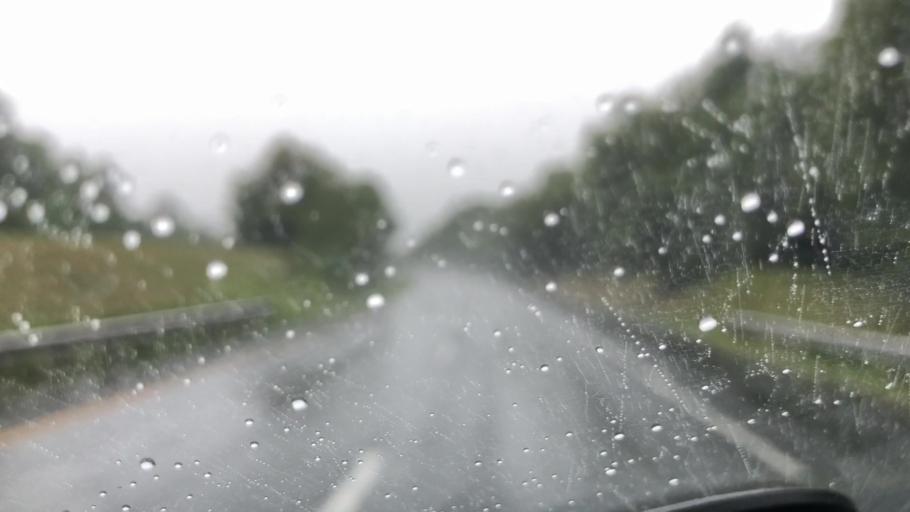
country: US
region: Massachusetts
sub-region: Hampden County
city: Westfield
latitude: 42.1562
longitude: -72.7758
